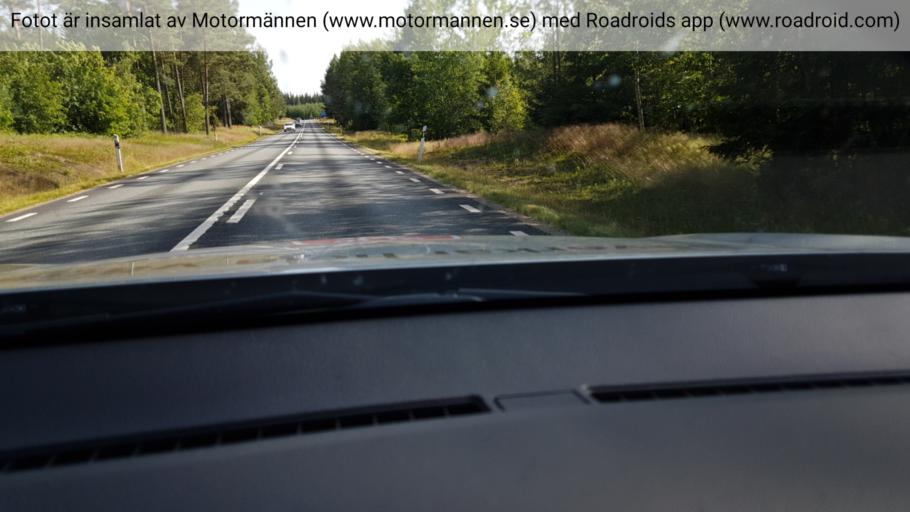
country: SE
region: Joenkoeping
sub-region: Vetlanda Kommun
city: Ekenassjon
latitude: 57.5200
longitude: 14.9883
